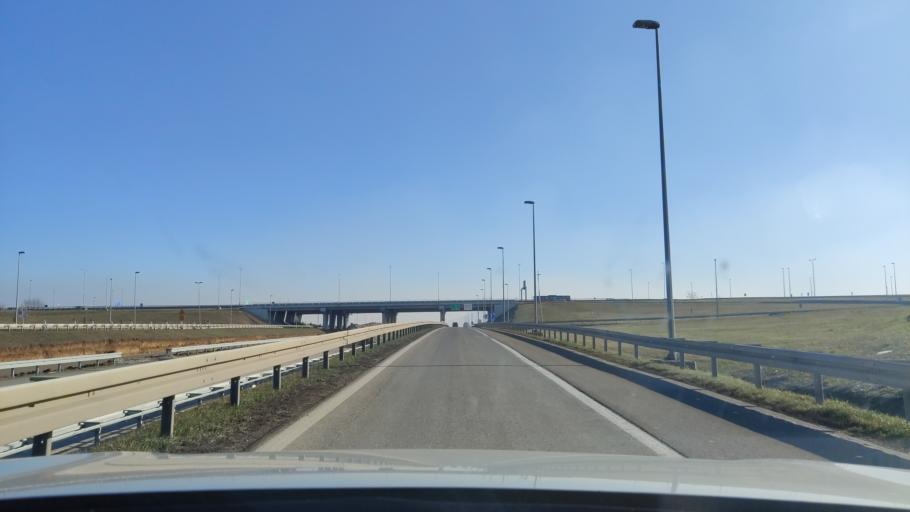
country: RS
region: Central Serbia
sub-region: Belgrade
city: Rakovica
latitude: 44.7137
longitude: 20.4127
